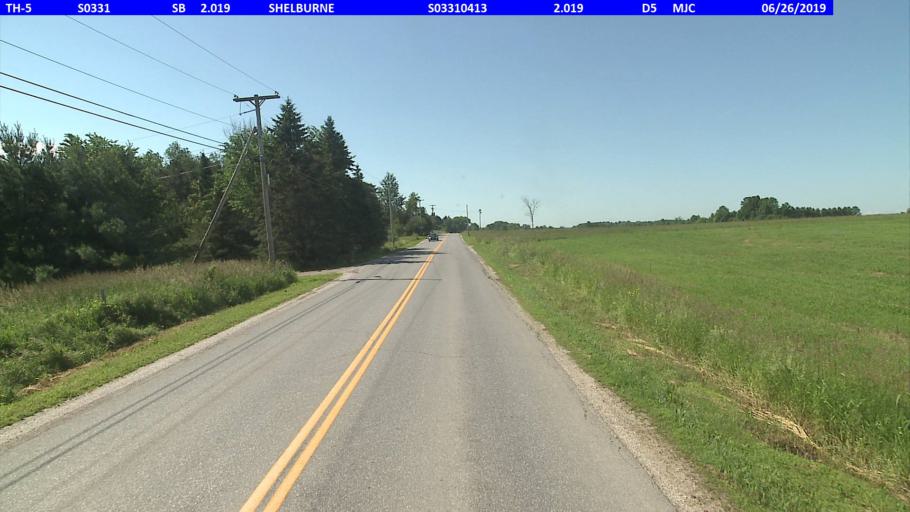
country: US
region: Vermont
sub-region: Chittenden County
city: South Burlington
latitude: 44.3996
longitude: -73.1770
